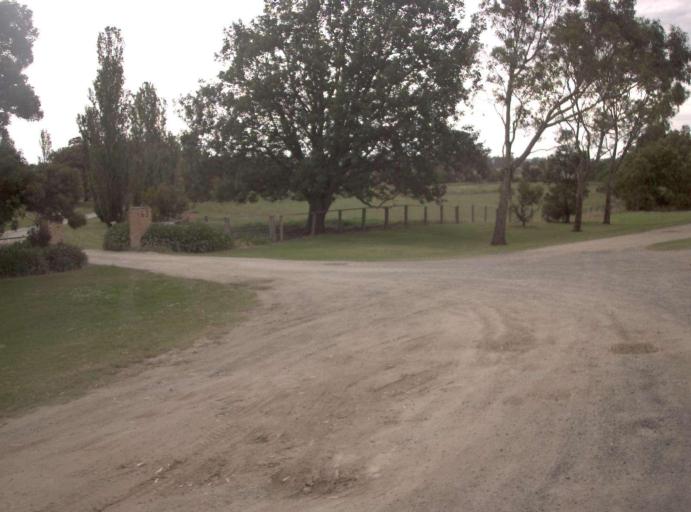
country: AU
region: Victoria
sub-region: Latrobe
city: Traralgon
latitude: -38.5519
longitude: 146.6818
